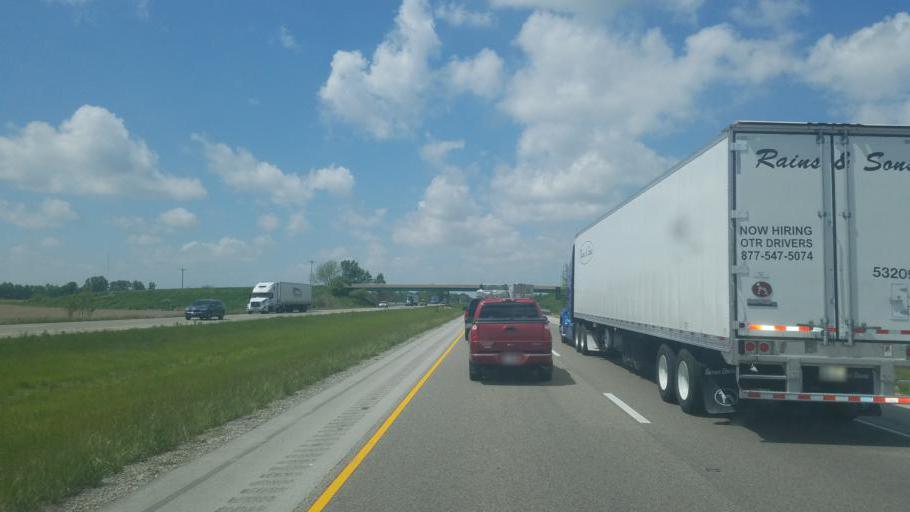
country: US
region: Illinois
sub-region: Cumberland County
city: Toledo
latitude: 39.2297
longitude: -88.2180
